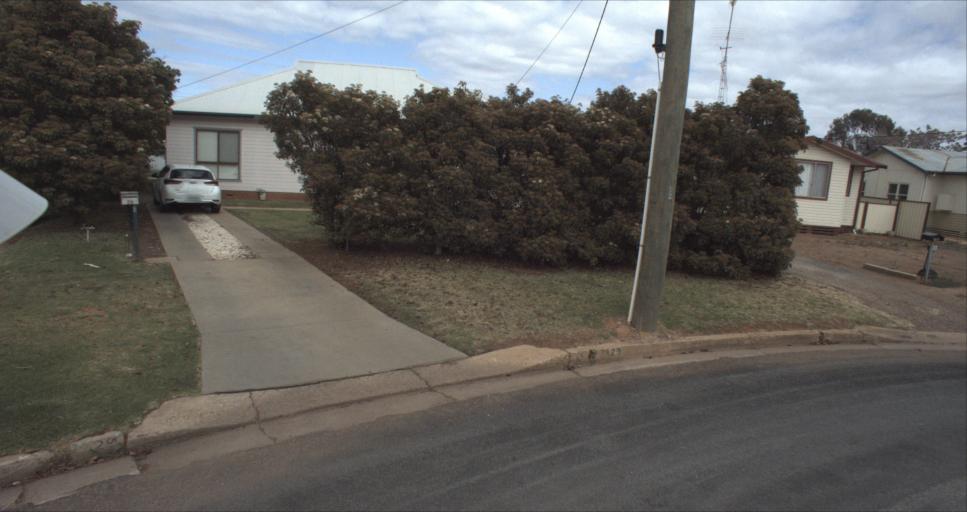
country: AU
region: New South Wales
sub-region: Leeton
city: Leeton
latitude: -34.5661
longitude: 146.3942
